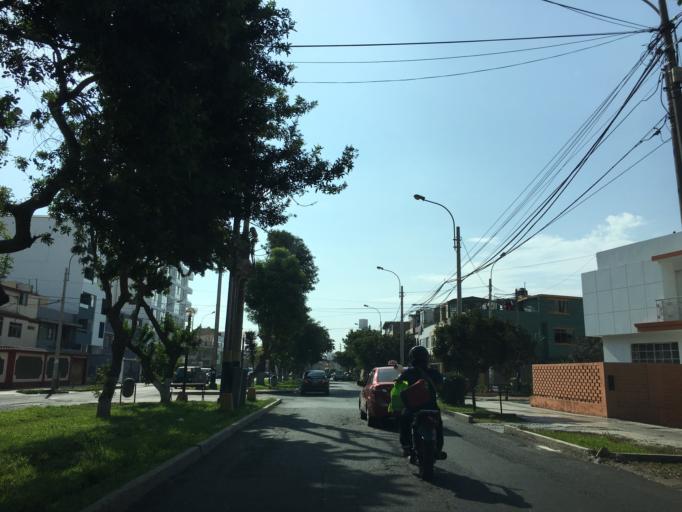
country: PE
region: Lima
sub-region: Lima
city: San Isidro
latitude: -12.0734
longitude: -77.0628
